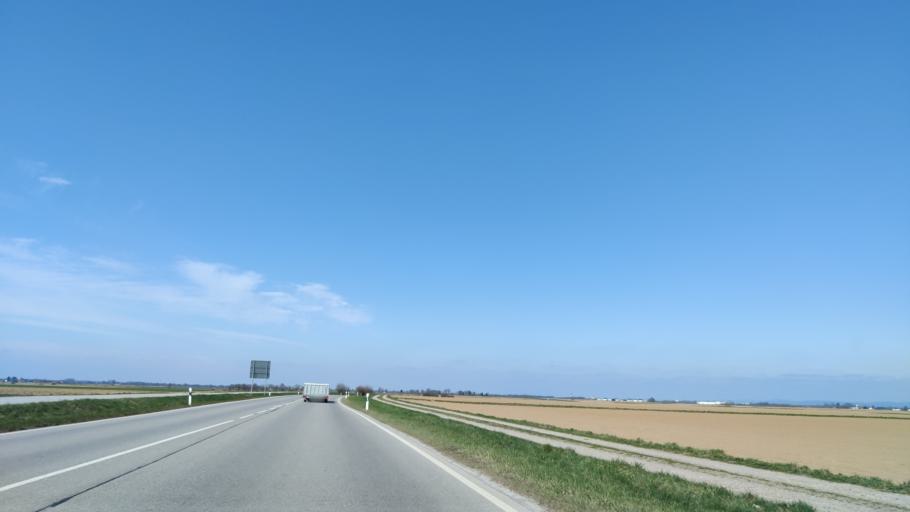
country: DE
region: Bavaria
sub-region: Lower Bavaria
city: Strasskirchen
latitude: 48.8399
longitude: 12.6815
